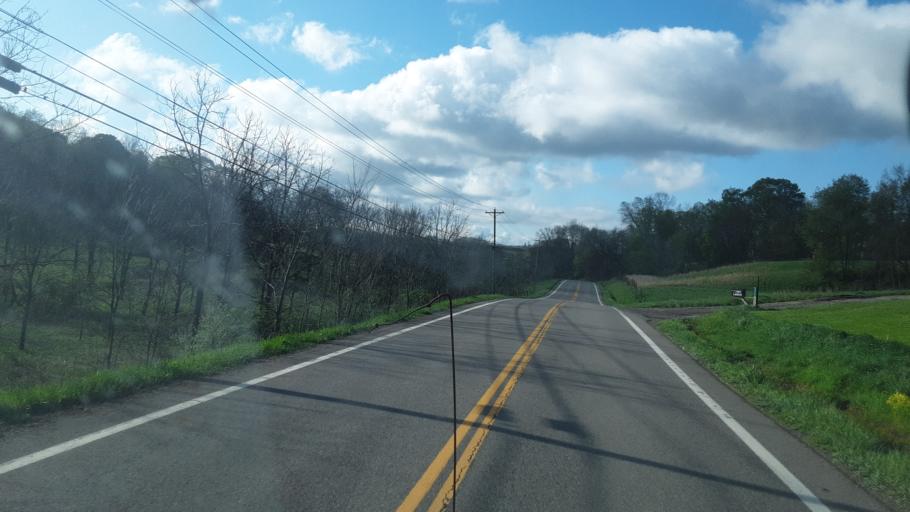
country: US
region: Ohio
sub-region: Muskingum County
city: New Concord
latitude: 39.9020
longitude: -81.6753
